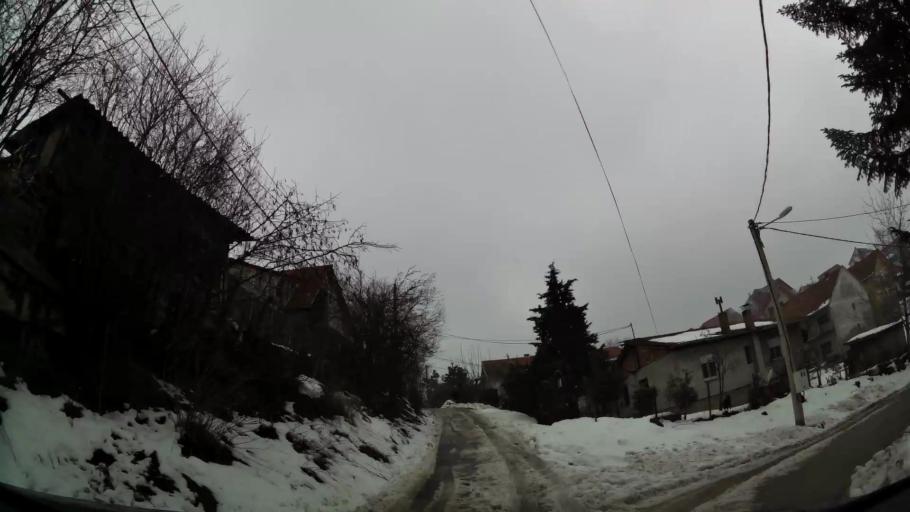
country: RS
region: Central Serbia
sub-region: Belgrade
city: Zvezdara
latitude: 44.7510
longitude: 20.5251
